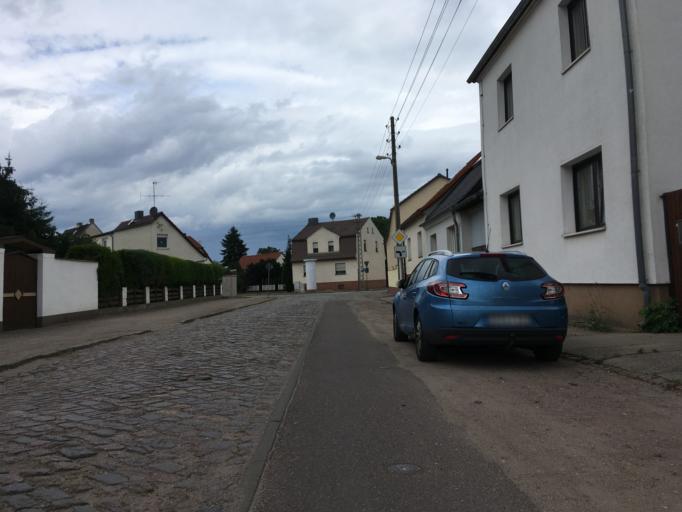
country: DE
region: Saxony-Anhalt
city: Quellendorf
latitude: 51.8105
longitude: 12.1542
